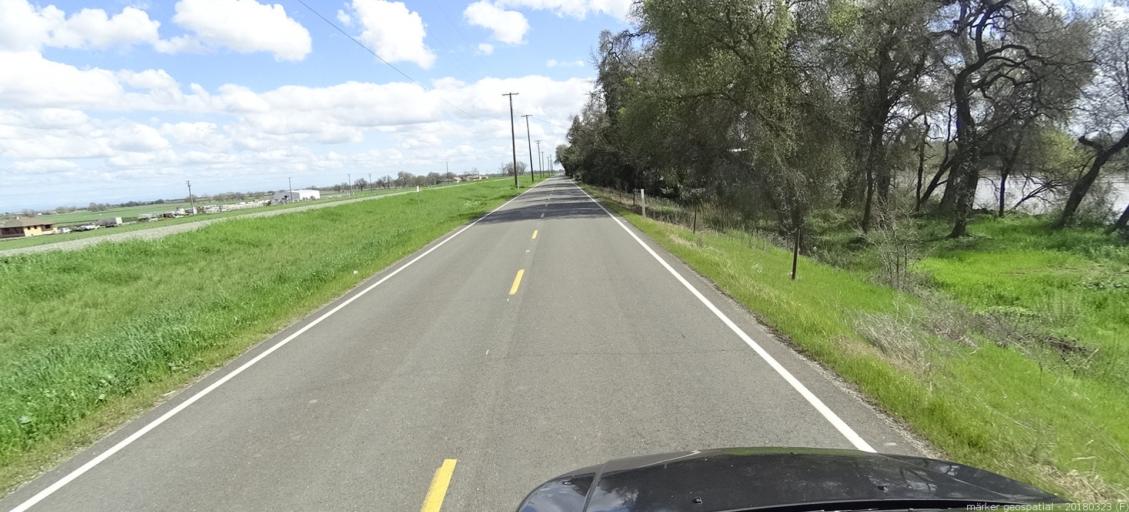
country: US
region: California
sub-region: Yolo County
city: West Sacramento
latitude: 38.6692
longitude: -121.6191
